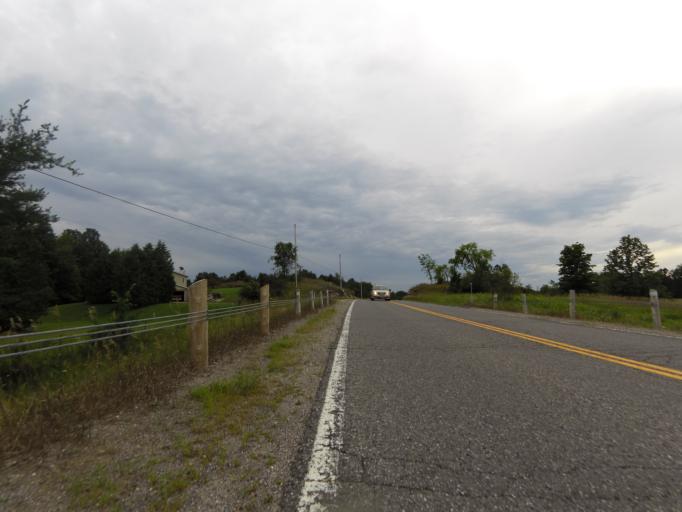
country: CA
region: Ontario
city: Carleton Place
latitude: 45.1306
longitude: -76.3320
